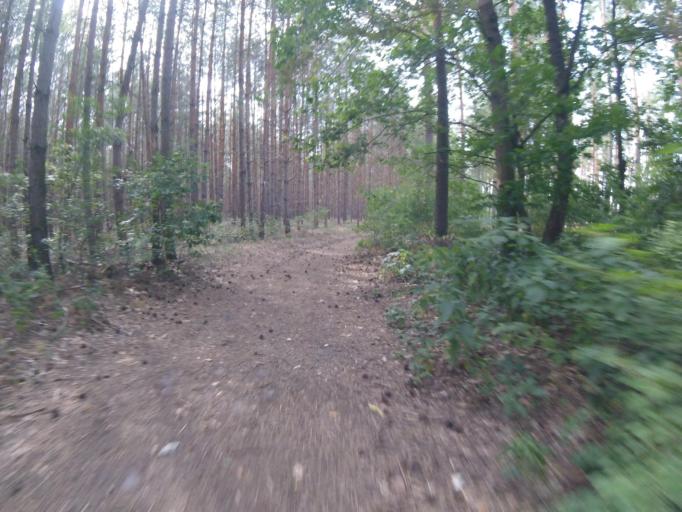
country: DE
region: Brandenburg
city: Wildau
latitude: 52.3088
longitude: 13.7222
